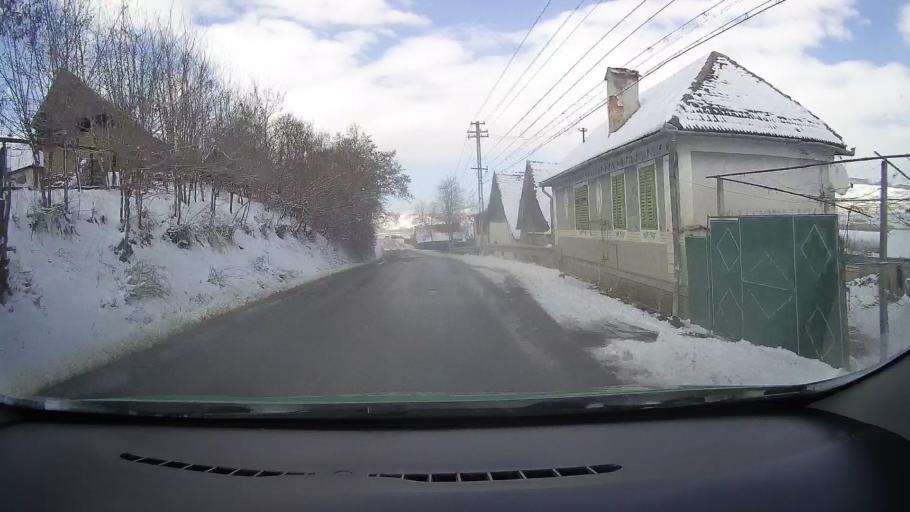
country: RO
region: Sibiu
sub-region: Comuna Altina
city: Altina
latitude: 45.9341
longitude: 24.4636
